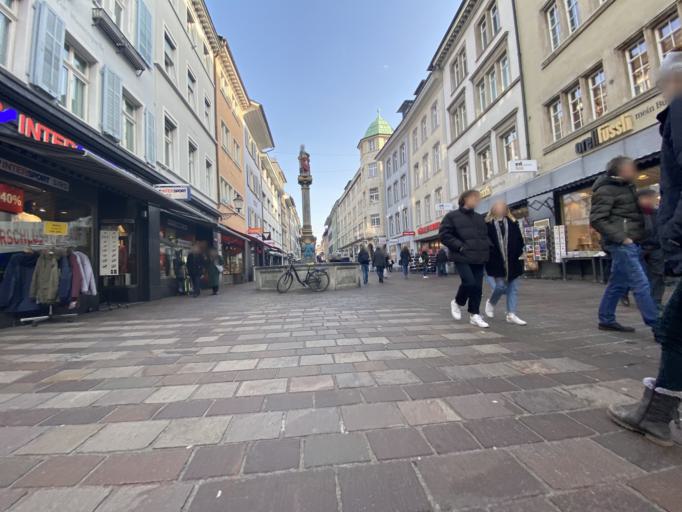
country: CH
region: Zurich
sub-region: Bezirk Winterthur
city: Stadt Winterthur (Kreis 1) / Altstadt
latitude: 47.4996
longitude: 8.7278
